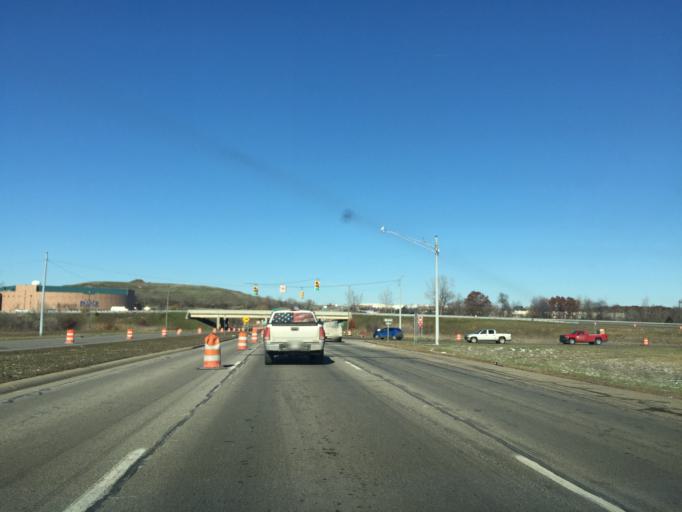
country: US
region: Michigan
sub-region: Oakland County
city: Auburn Hills
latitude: 42.6912
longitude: -83.2413
